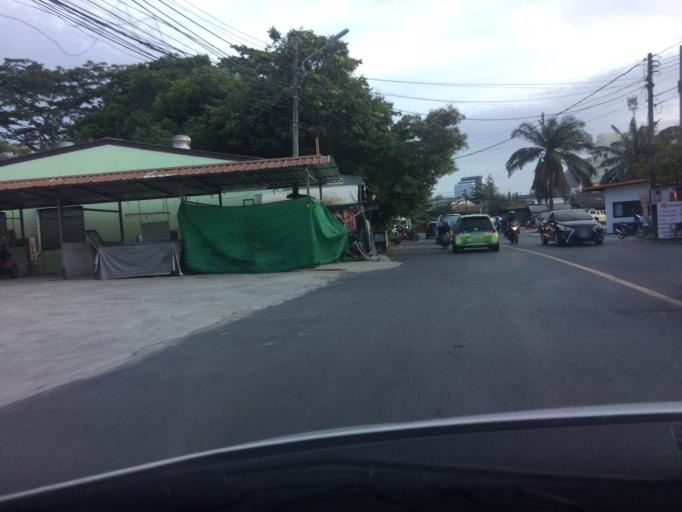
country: TH
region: Phuket
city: Ban Talat Yai
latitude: 7.8743
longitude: 98.3978
